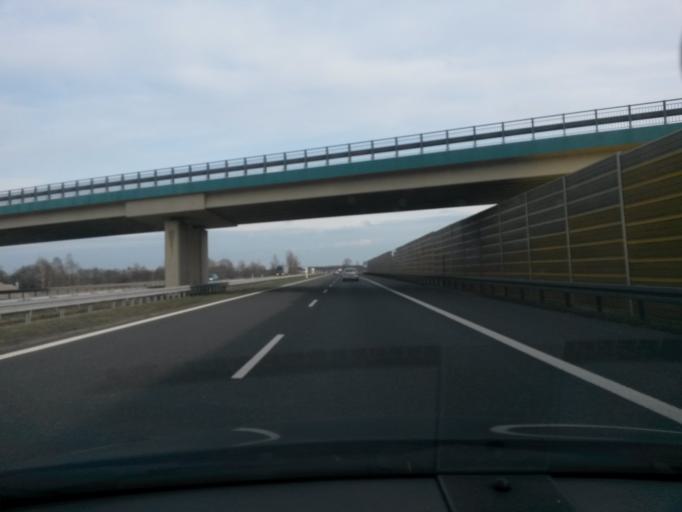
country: PL
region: Greater Poland Voivodeship
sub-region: Powiat kolski
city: Dabie
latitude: 52.0485
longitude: 18.8509
